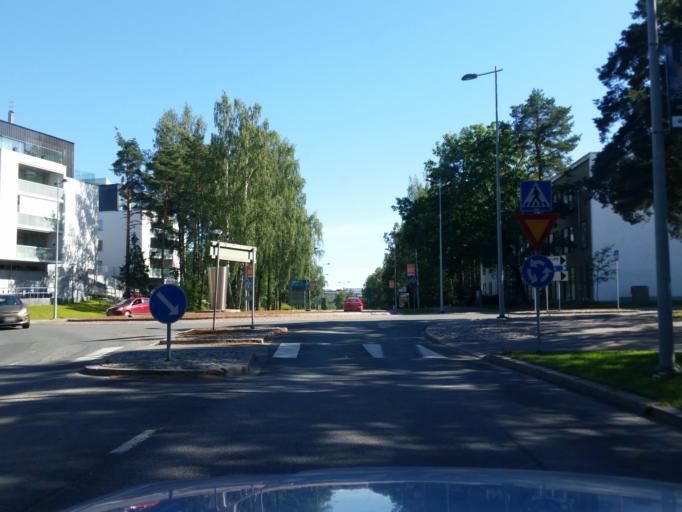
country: FI
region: Uusimaa
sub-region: Helsinki
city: Otaniemi
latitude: 60.1791
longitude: 24.7984
